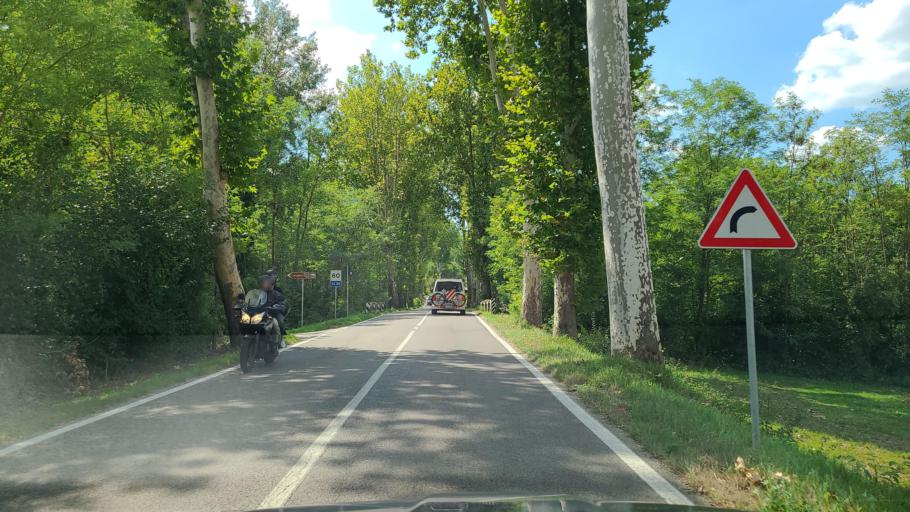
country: IT
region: Tuscany
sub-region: Provincia di Siena
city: Colle di Val d'Elsa
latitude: 43.4108
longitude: 11.0681
